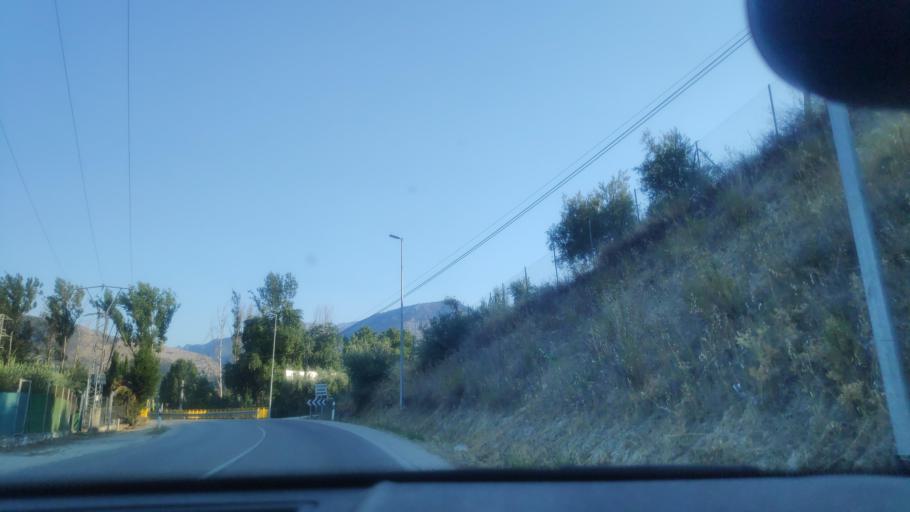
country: ES
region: Andalusia
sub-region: Provincia de Jaen
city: Jaen
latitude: 37.7213
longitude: -3.7644
